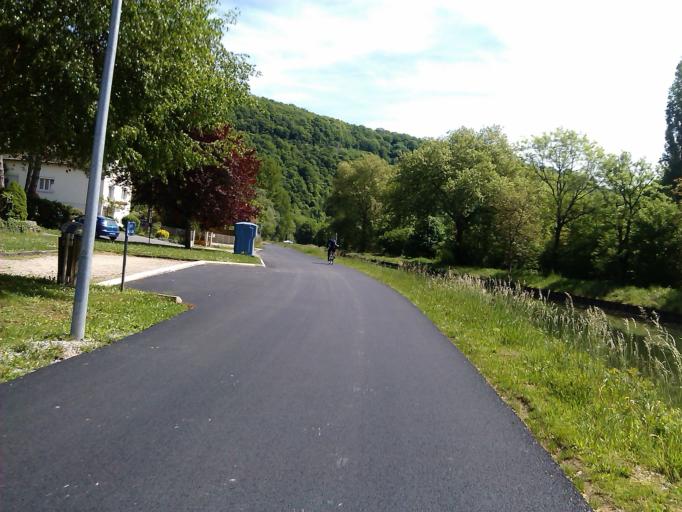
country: FR
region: Franche-Comte
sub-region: Departement du Doubs
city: Avanne-Aveney
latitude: 47.1938
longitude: 5.9597
